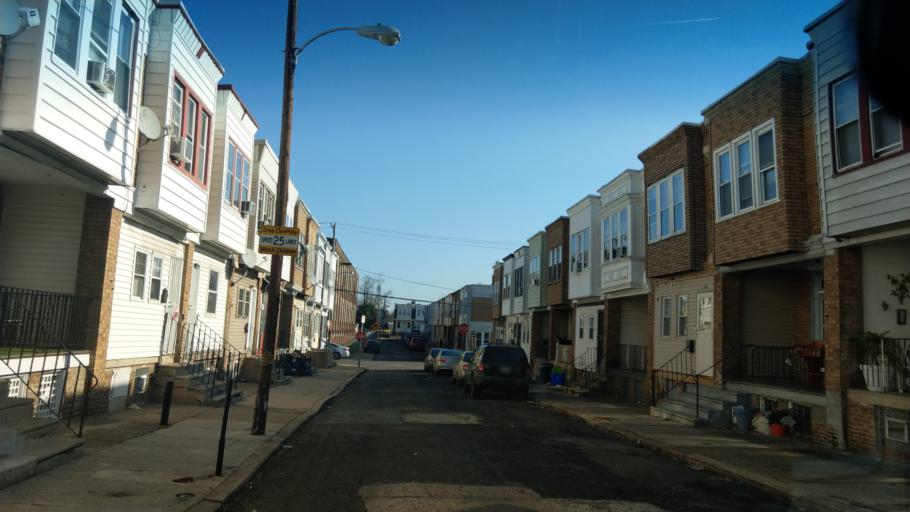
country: US
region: Pennsylvania
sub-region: Montgomery County
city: Rockledge
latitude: 40.0321
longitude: -75.1293
